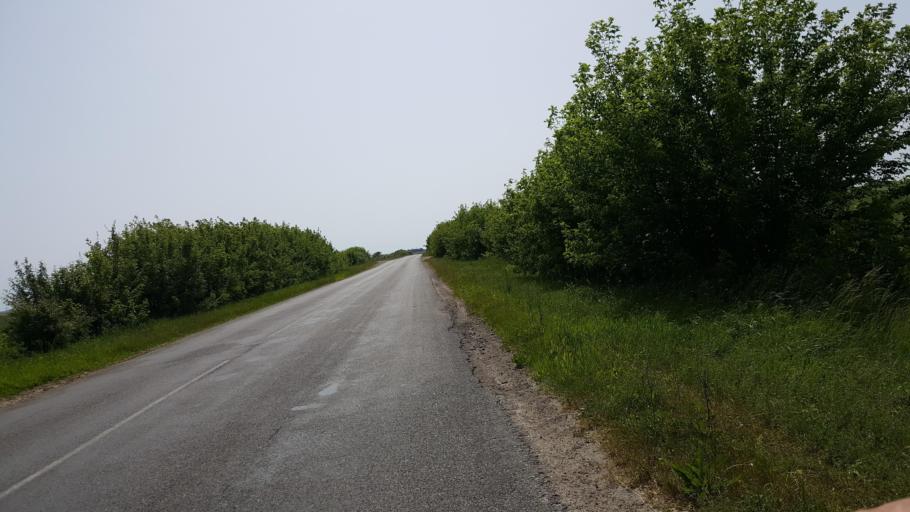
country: BY
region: Brest
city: Kamyanyets
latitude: 52.4294
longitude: 23.8190
